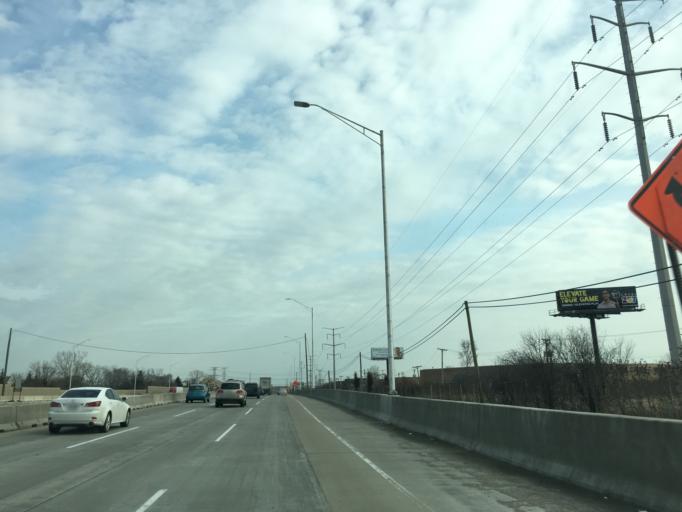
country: US
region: Illinois
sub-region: Cook County
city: Elk Grove Village
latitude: 42.0344
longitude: -87.9728
